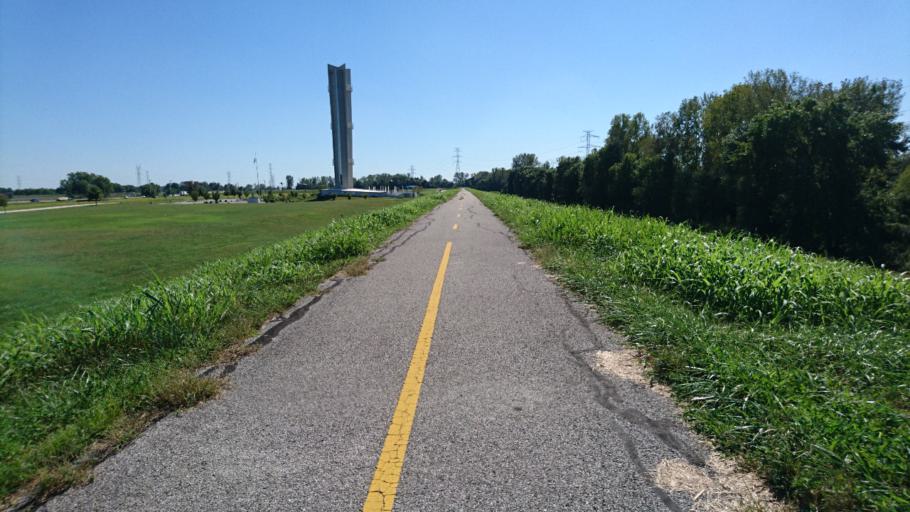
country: US
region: Illinois
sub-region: Madison County
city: Hartford
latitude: 38.8134
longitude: -90.1005
